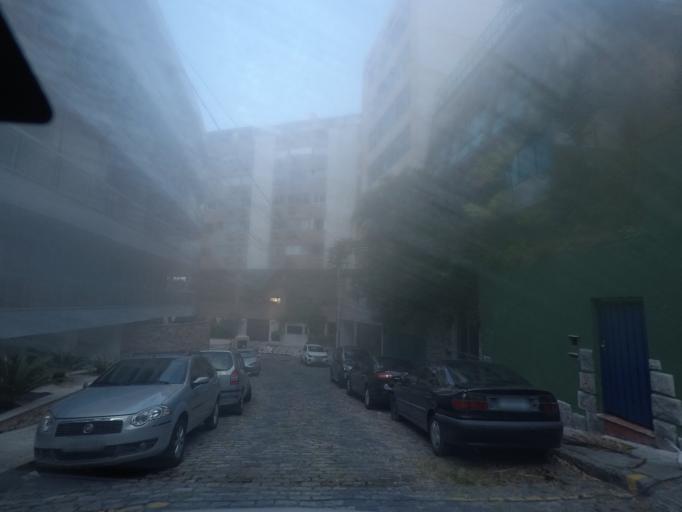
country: BR
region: Rio de Janeiro
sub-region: Rio De Janeiro
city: Rio de Janeiro
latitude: -22.9631
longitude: -43.2016
